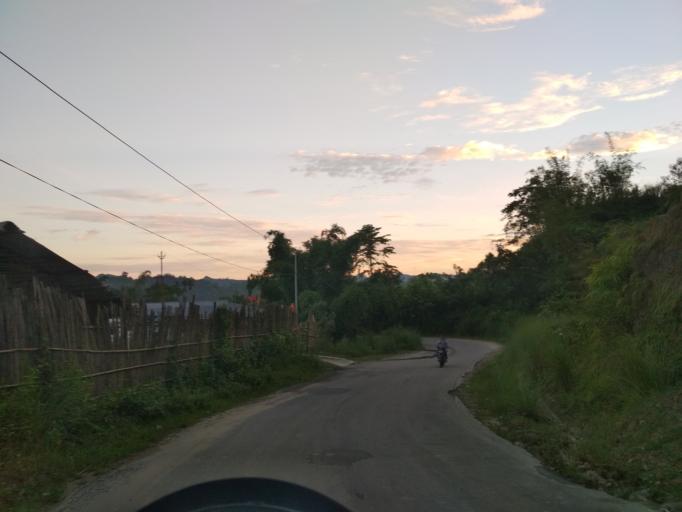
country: IN
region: Arunachal Pradesh
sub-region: Papum Pare
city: Naharlagun
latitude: 27.0866
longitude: 93.6686
